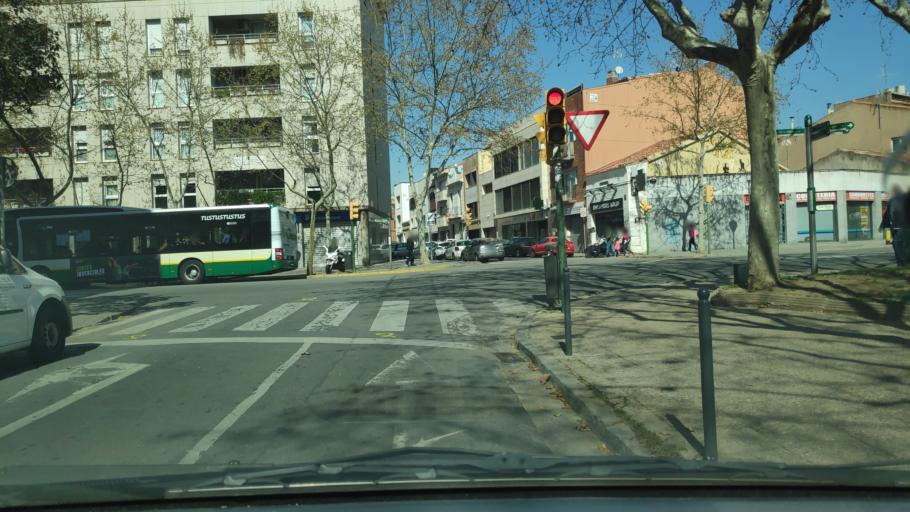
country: ES
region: Catalonia
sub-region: Provincia de Barcelona
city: Sabadell
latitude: 41.5512
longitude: 2.1037
